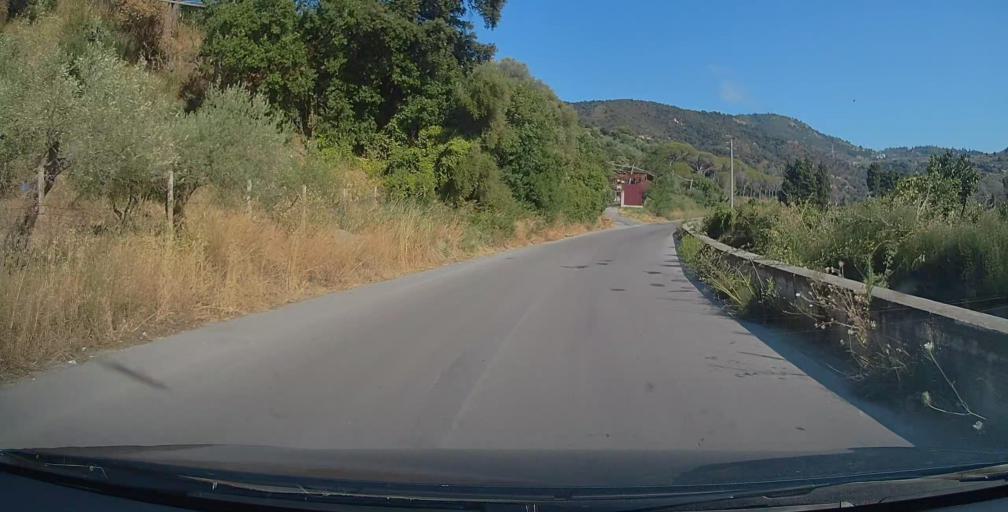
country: IT
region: Sicily
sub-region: Messina
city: Patti
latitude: 38.1365
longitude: 14.9993
